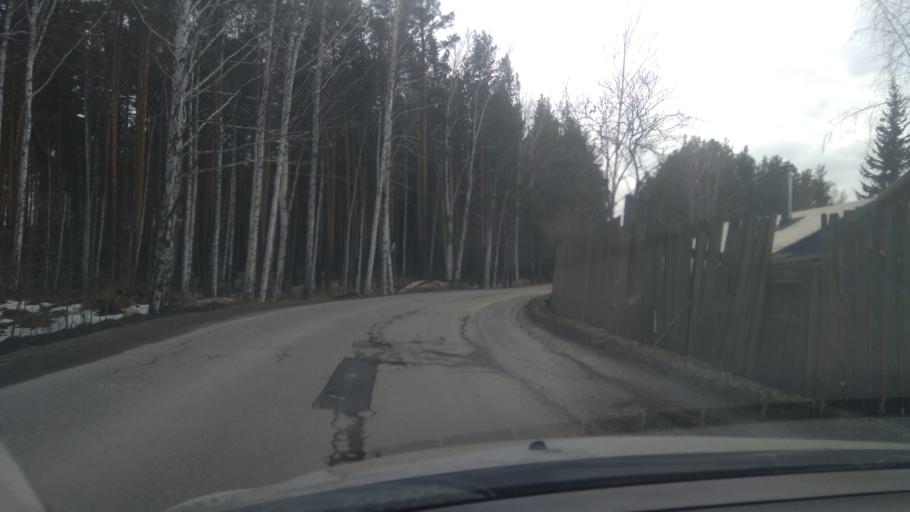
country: RU
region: Sverdlovsk
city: Severka
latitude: 56.8408
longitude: 60.3855
